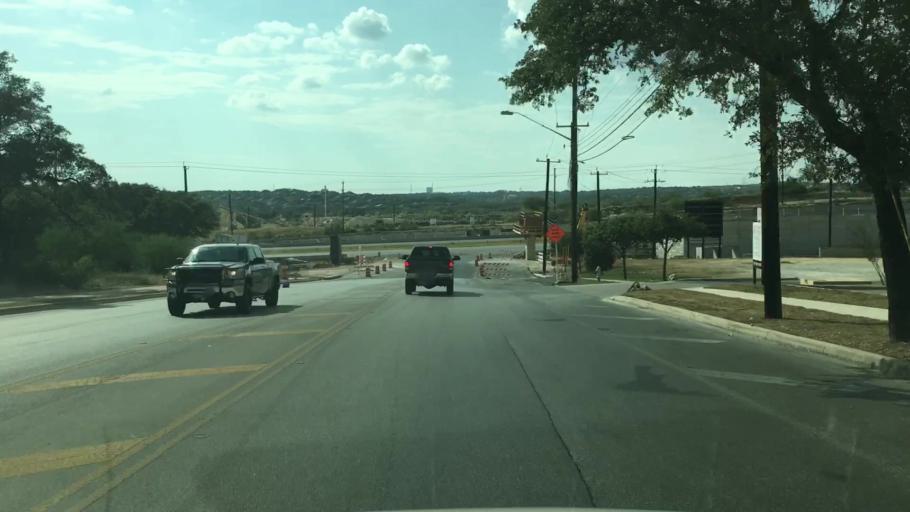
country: US
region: Texas
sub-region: Bexar County
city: Hollywood Park
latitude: 29.6209
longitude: -98.4630
